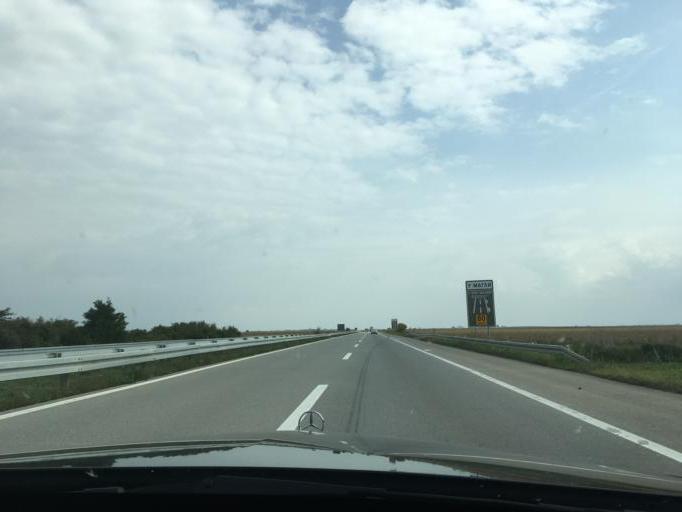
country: RS
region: Autonomna Pokrajina Vojvodina
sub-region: Sremski Okrug
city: Sremska Mitrovica
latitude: 44.9984
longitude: 19.6645
